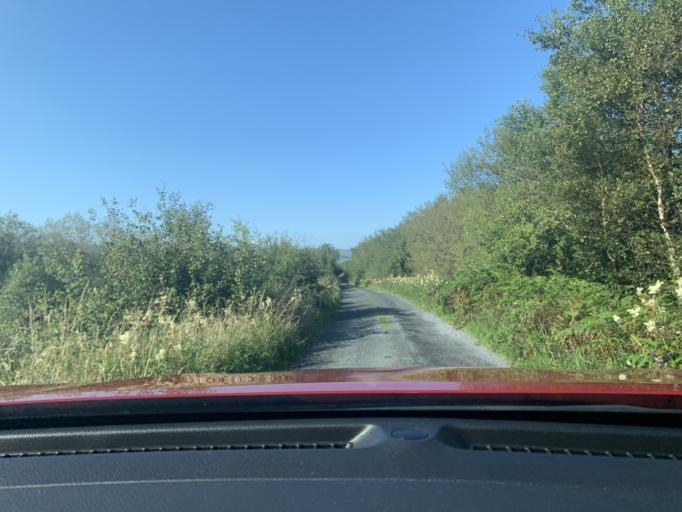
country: IE
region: Connaught
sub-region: Sligo
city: Tobercurry
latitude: 54.0688
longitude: -8.7775
